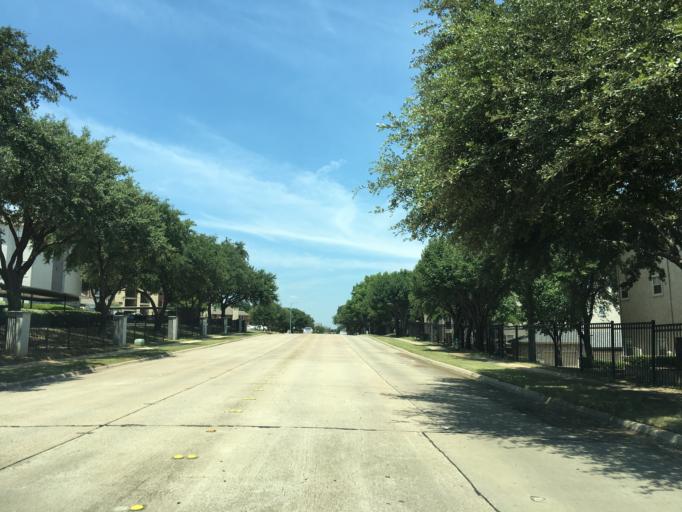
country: US
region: Texas
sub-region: Denton County
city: Lewisville
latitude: 33.0114
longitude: -96.9860
